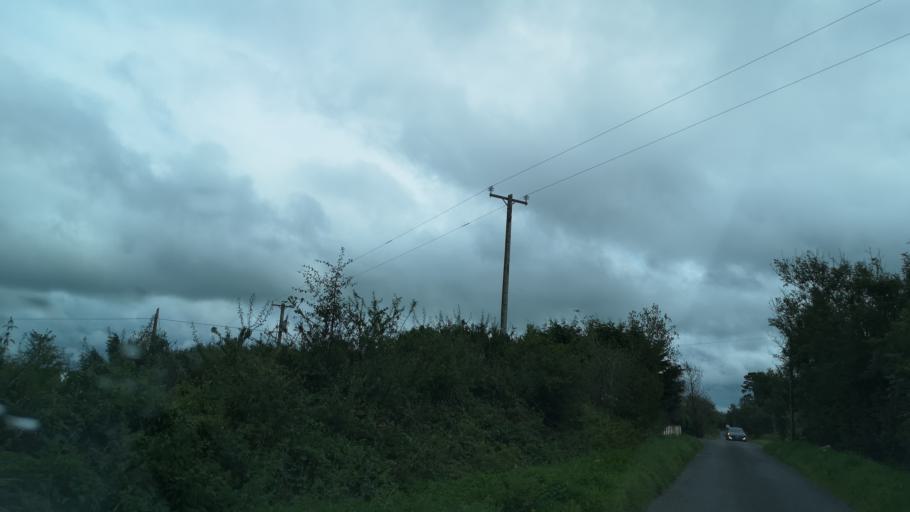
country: IE
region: Connaught
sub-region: County Galway
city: Loughrea
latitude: 53.2986
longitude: -8.5951
